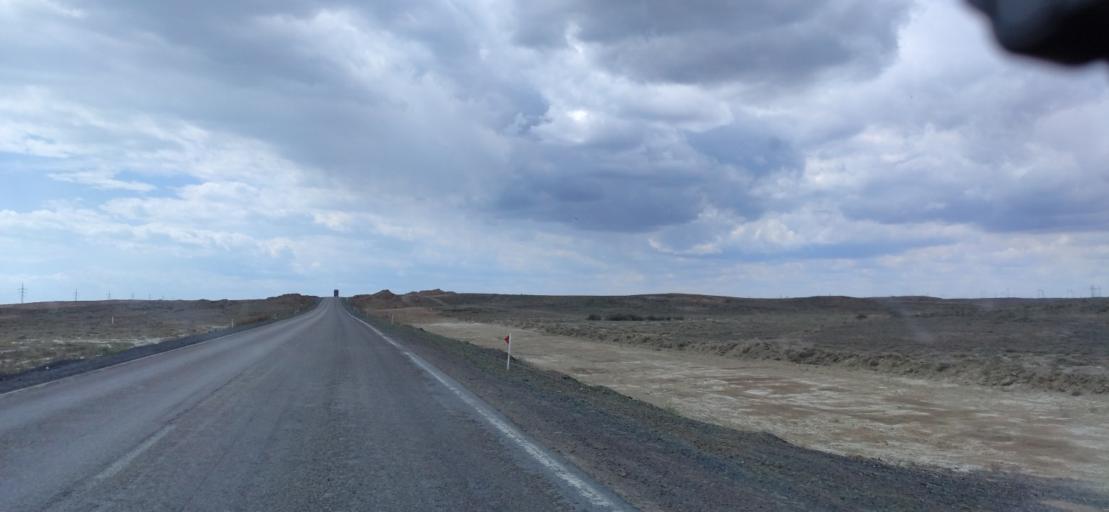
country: KZ
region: Qaraghandy
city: Saryshaghan
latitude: 46.0872
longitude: 73.6063
